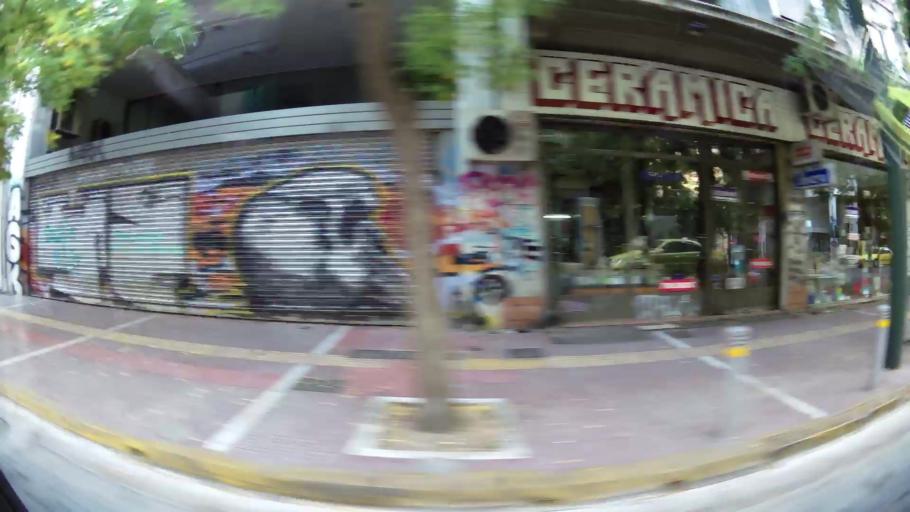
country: GR
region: Attica
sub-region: Nomarchia Athinas
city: Athens
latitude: 37.9873
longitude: 23.7288
